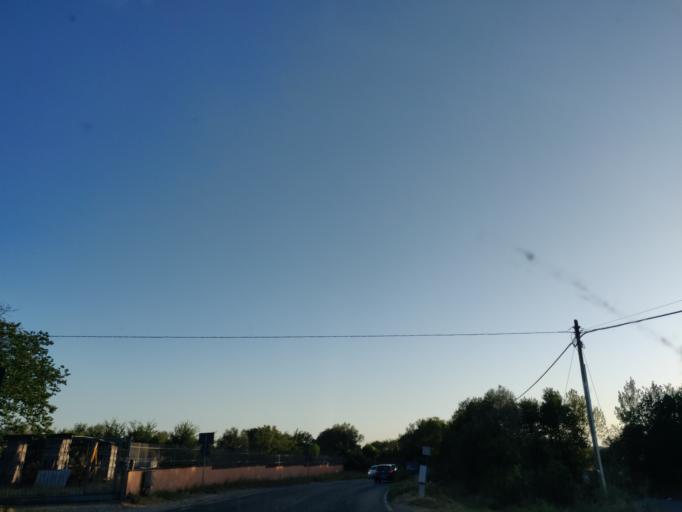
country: IT
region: Latium
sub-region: Provincia di Viterbo
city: Canino
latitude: 42.4593
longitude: 11.7427
